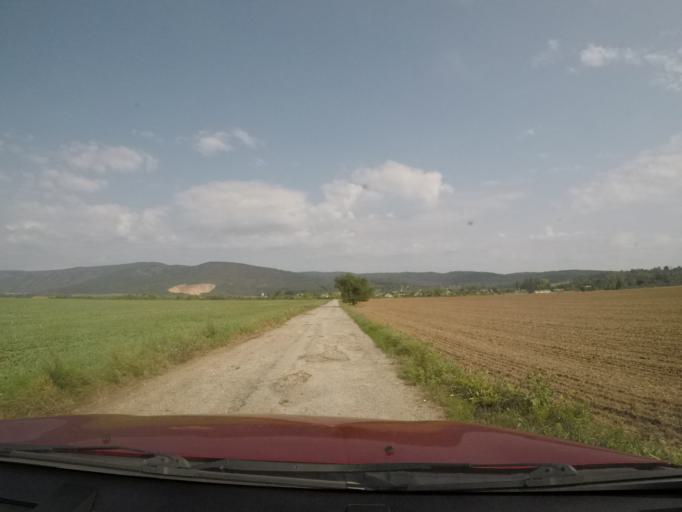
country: SK
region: Kosicky
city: Moldava nad Bodvou
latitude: 48.5999
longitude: 20.9540
